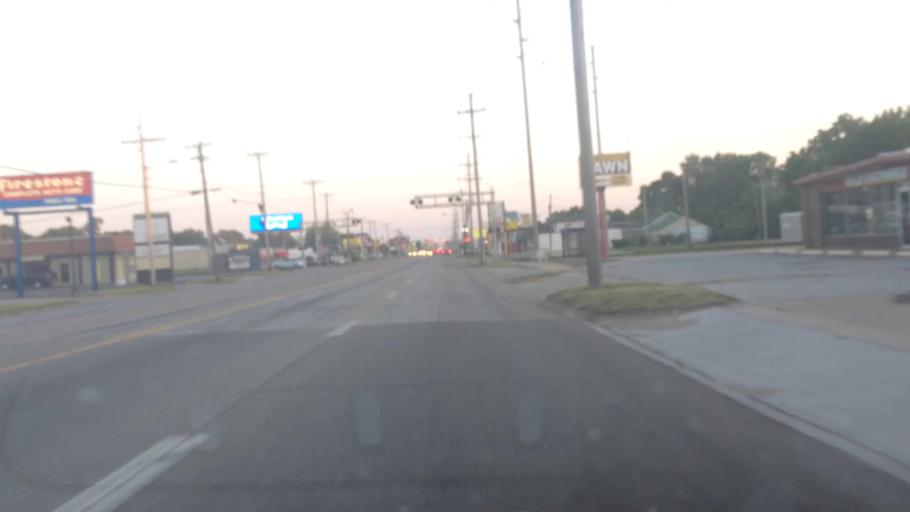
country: US
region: Missouri
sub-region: Greene County
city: Springfield
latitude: 37.1999
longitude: -93.2621
